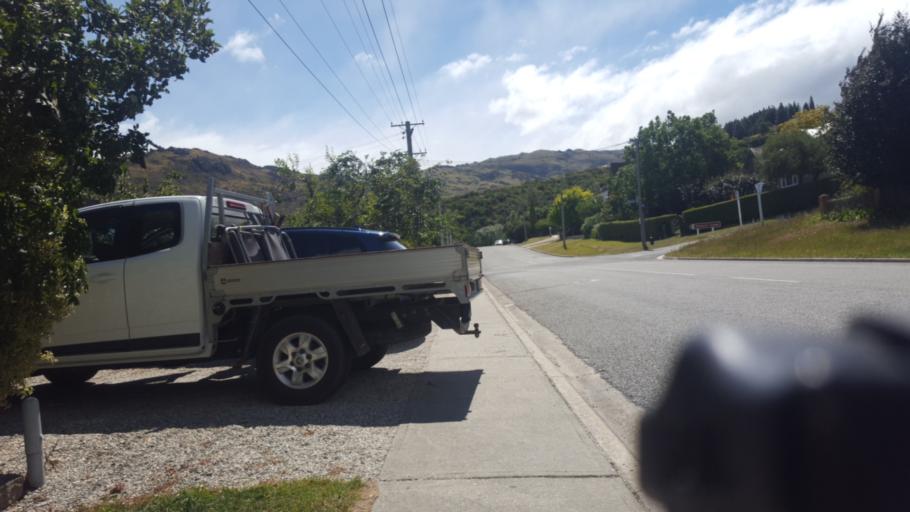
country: NZ
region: Otago
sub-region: Queenstown-Lakes District
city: Wanaka
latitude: -45.1859
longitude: 169.3192
